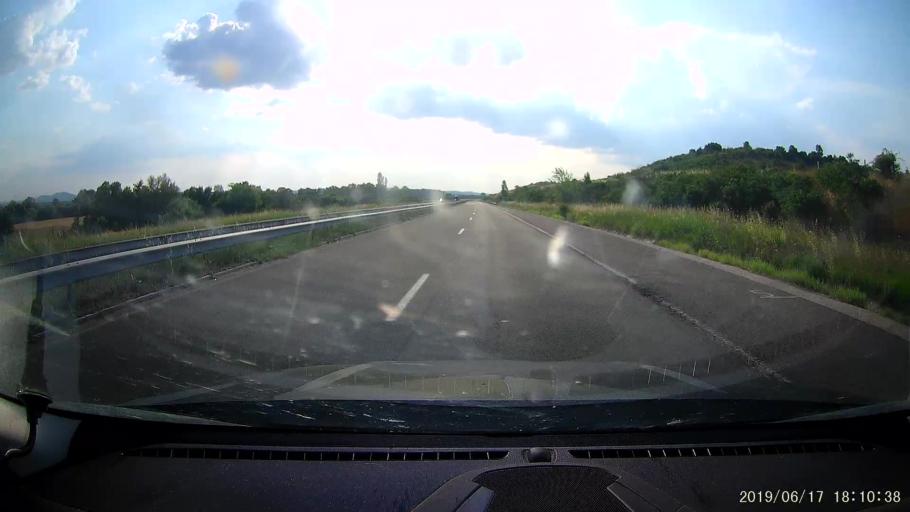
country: BG
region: Khaskovo
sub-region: Obshtina Lyubimets
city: Lyubimets
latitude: 41.8762
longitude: 26.0725
